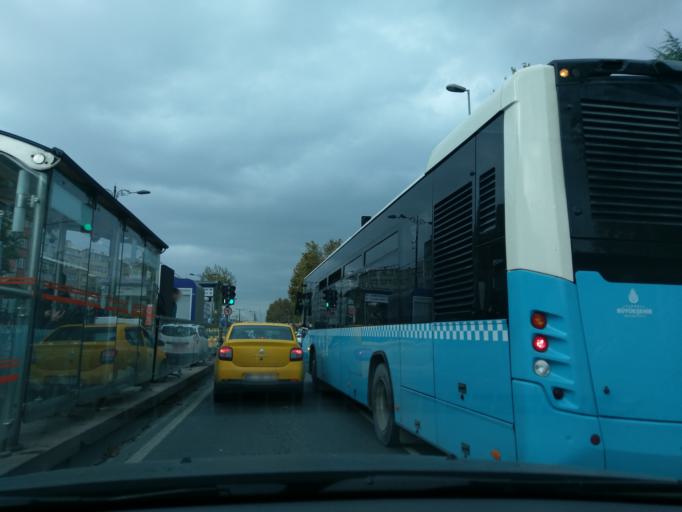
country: TR
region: Istanbul
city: Istanbul
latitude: 41.0154
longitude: 28.9333
